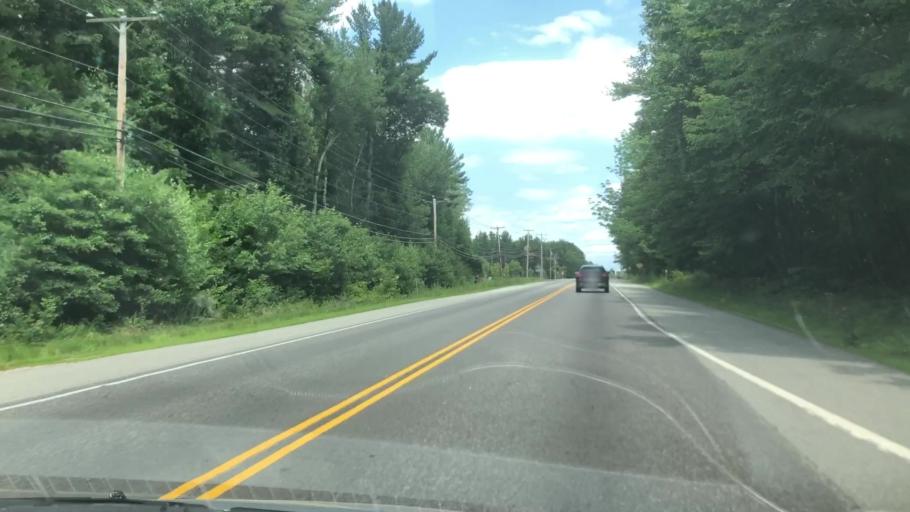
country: US
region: New Hampshire
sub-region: Hillsborough County
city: Bedford
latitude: 42.9167
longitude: -71.5466
